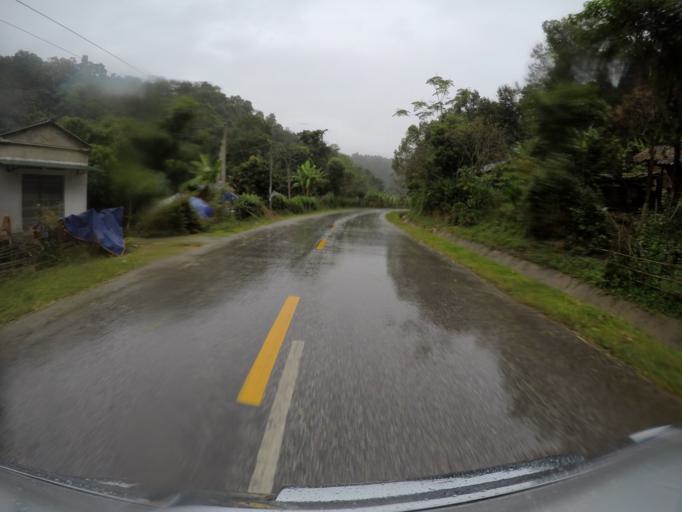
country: VN
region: Lai Chau
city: Than Uyen
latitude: 22.0918
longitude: 103.8364
